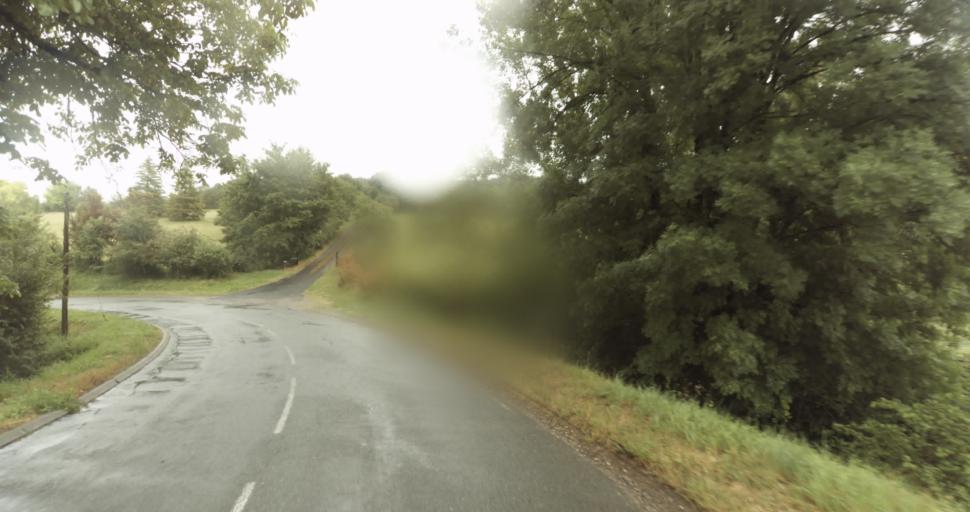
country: FR
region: Aquitaine
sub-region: Departement de la Dordogne
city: Le Bugue
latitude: 44.8255
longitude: 0.8916
